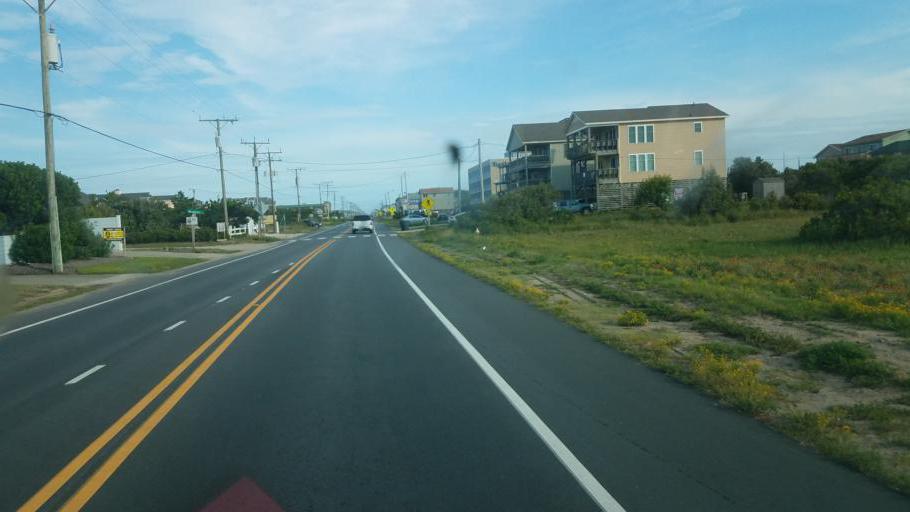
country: US
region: North Carolina
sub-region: Dare County
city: Kill Devil Hills
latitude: 36.0209
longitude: -75.6615
